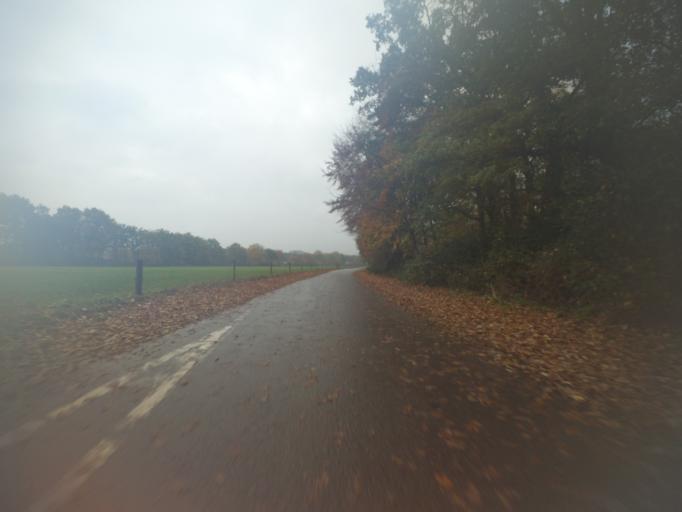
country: NL
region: Gelderland
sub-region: Gemeente Ede
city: Lunteren
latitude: 52.1066
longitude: 5.6407
